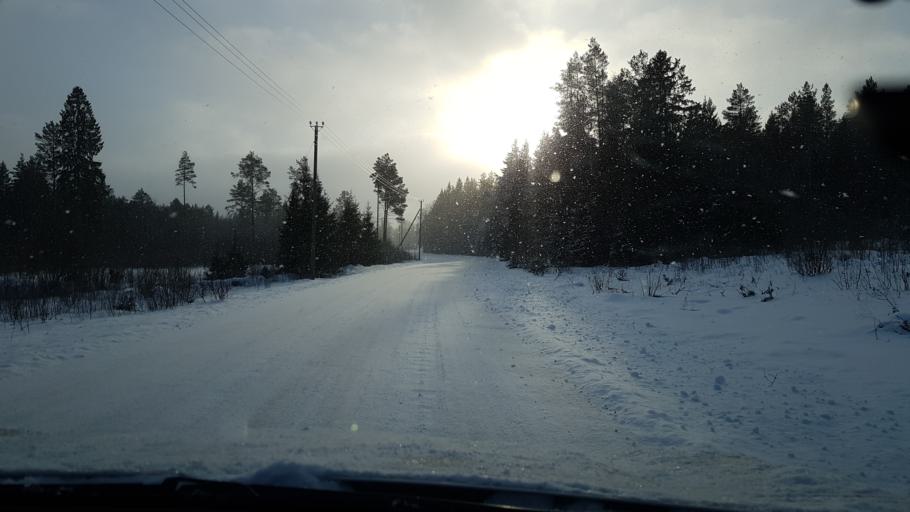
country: EE
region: Harju
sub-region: Nissi vald
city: Turba
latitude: 59.1930
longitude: 24.1400
